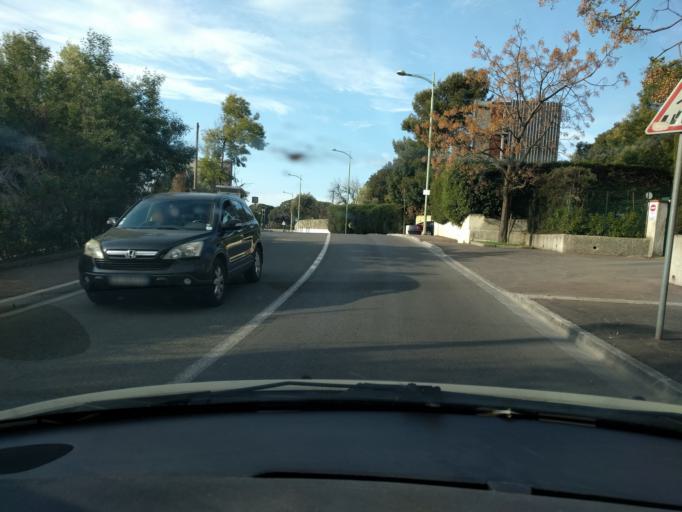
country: FR
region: Provence-Alpes-Cote d'Azur
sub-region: Departement des Alpes-Maritimes
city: Cannes
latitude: 43.5651
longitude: 6.9779
